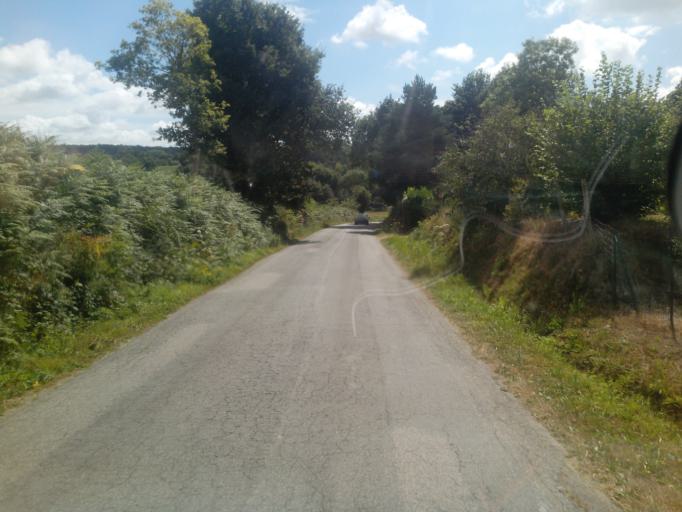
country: FR
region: Brittany
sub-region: Departement du Morbihan
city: Molac
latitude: 47.7197
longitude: -2.4305
